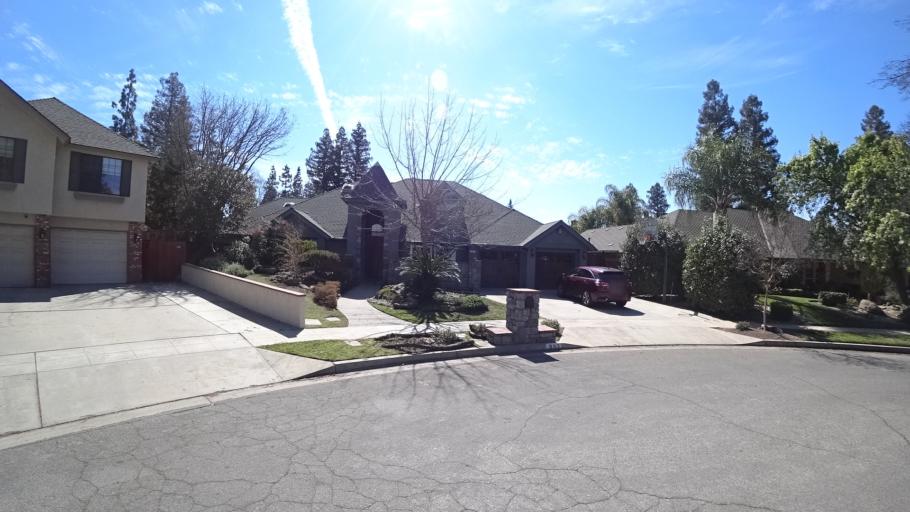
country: US
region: California
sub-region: Fresno County
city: Clovis
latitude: 36.8576
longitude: -119.7664
